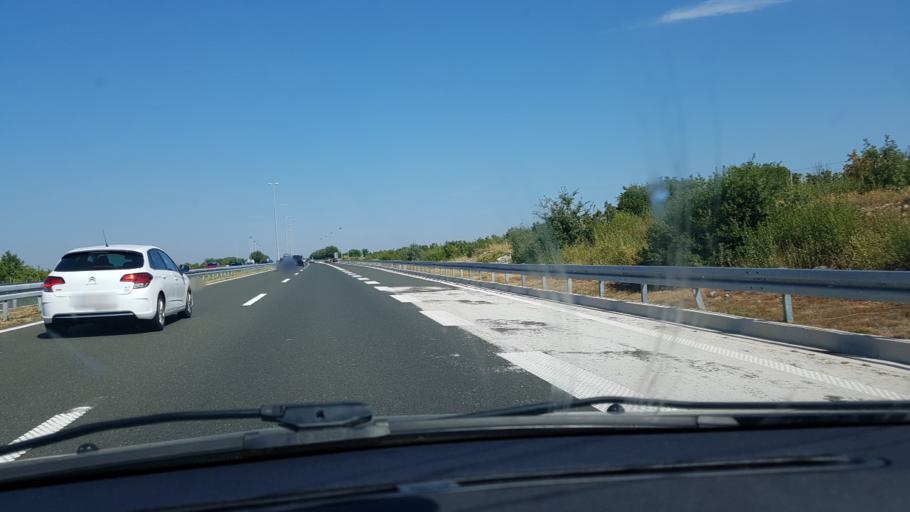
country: HR
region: Sibensko-Kniniska
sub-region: Grad Sibenik
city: Pirovac
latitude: 43.9416
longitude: 15.7000
